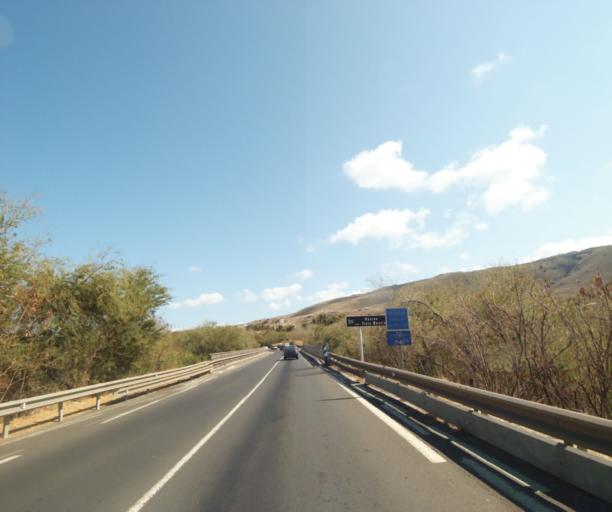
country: RE
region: Reunion
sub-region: Reunion
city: Trois-Bassins
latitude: -21.1102
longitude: 55.2560
